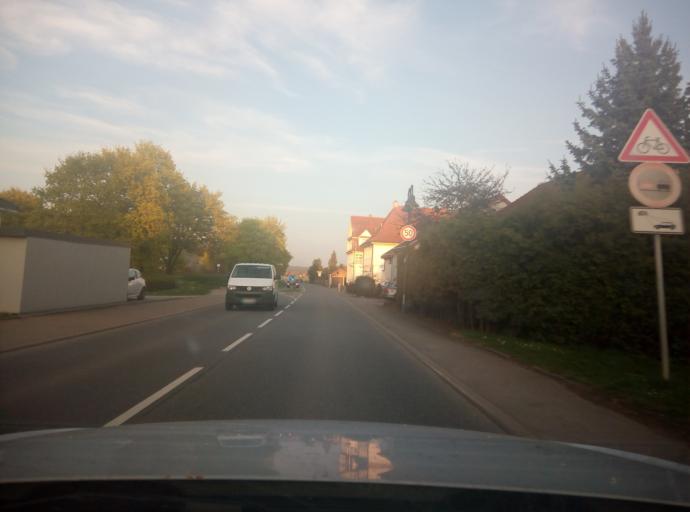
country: DE
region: Baden-Wuerttemberg
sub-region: Tuebingen Region
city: Rottenburg
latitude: 48.5011
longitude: 8.9677
